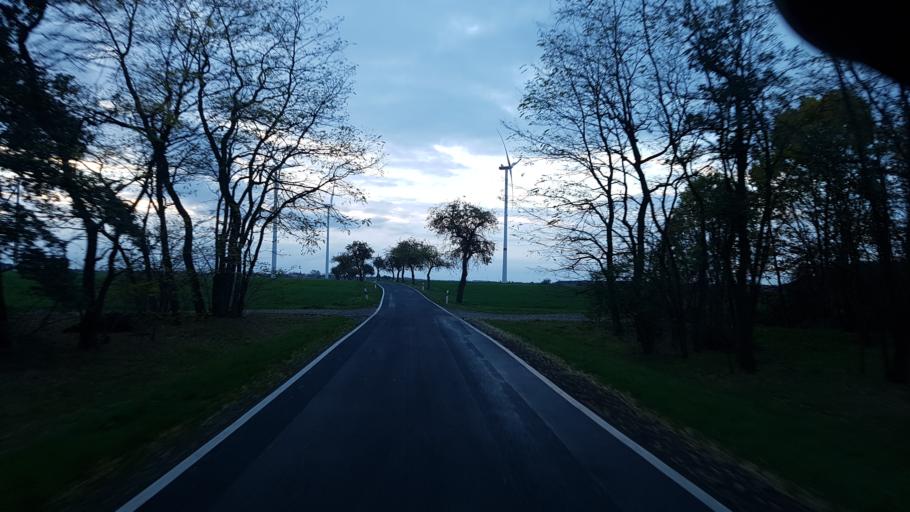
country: DE
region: Brandenburg
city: Muhlberg
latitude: 51.4732
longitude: 13.2395
